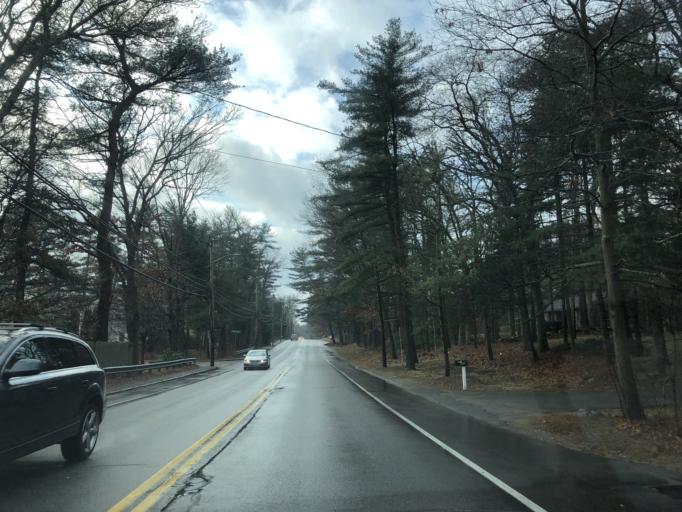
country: US
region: Massachusetts
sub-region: Bristol County
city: Attleboro
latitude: 41.9851
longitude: -71.2906
